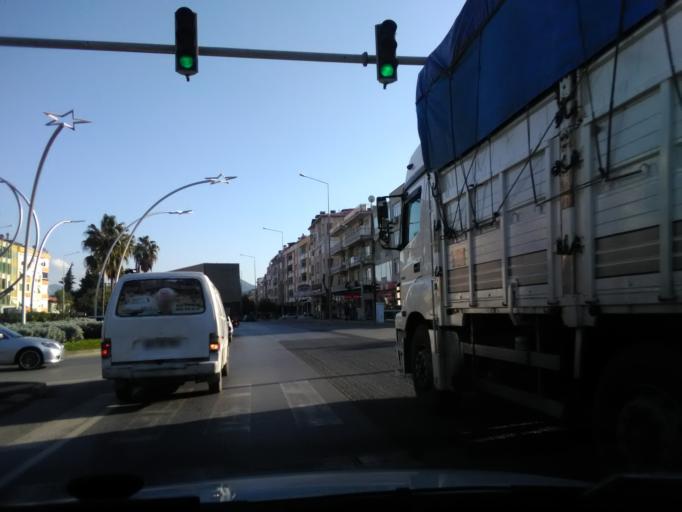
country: TR
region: Antalya
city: Gazipasa
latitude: 36.2730
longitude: 32.3097
